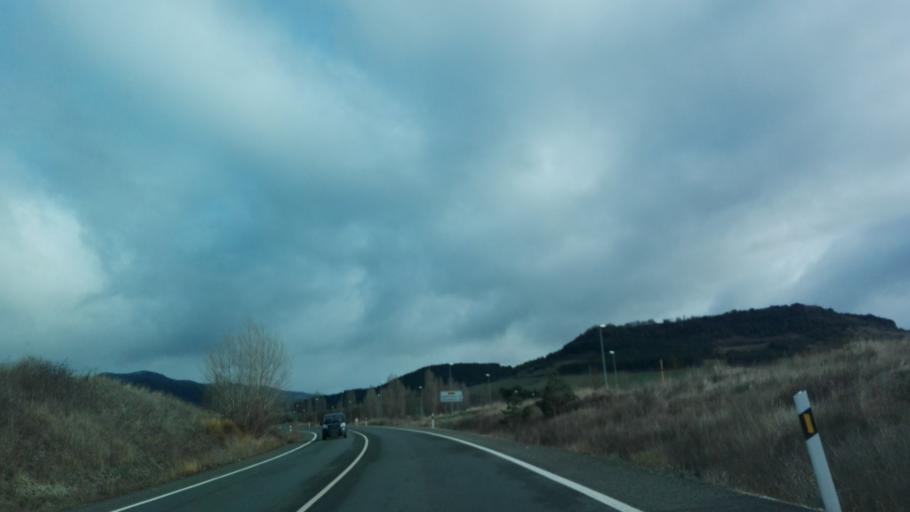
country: ES
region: Navarre
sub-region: Provincia de Navarra
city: Egues-Uharte
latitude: 42.8225
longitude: -1.5533
